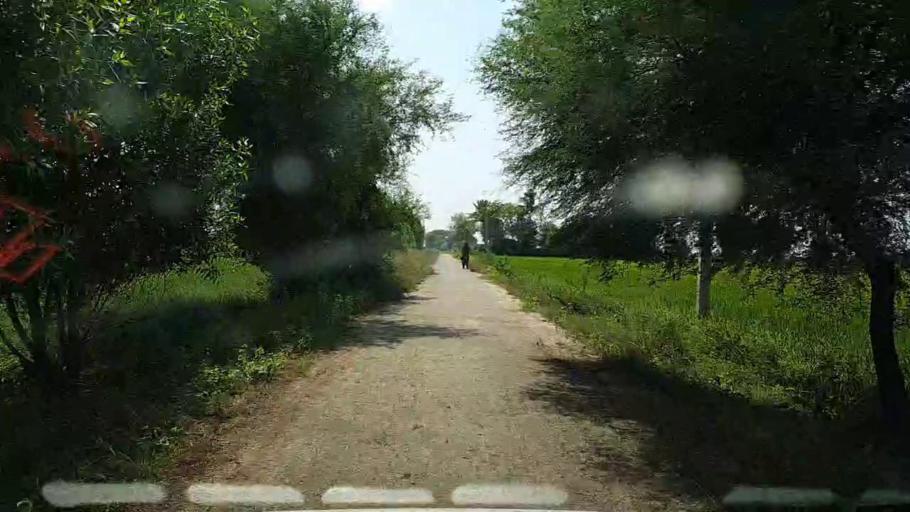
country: PK
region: Sindh
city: Kario
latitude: 24.6270
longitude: 68.5320
